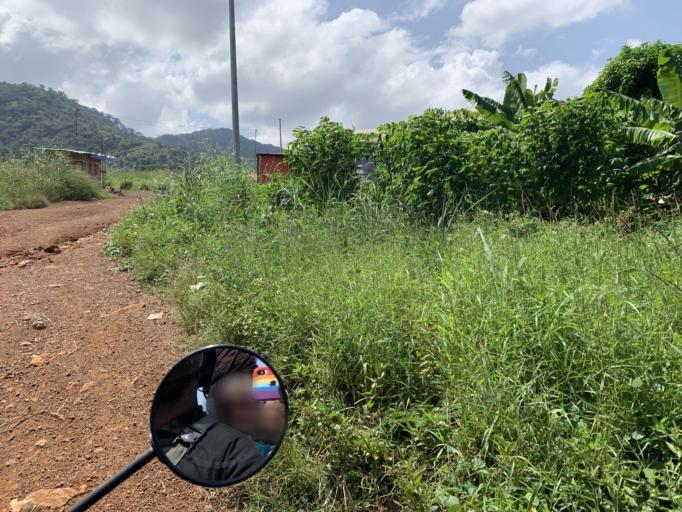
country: SL
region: Western Area
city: Hastings
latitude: 8.3719
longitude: -13.1346
